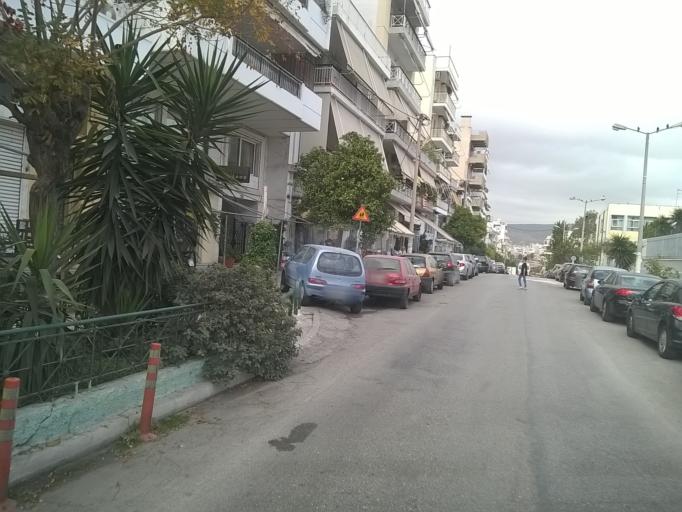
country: GR
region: Attica
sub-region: Nomos Attikis
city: Piraeus
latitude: 37.9351
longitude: 23.6310
